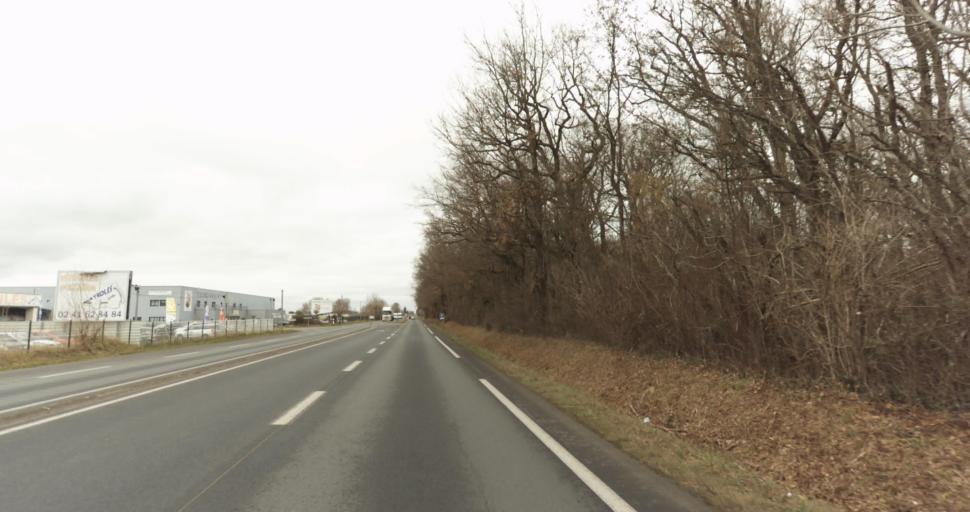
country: FR
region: Pays de la Loire
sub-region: Departement de Maine-et-Loire
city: Vivy
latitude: 47.3373
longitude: -0.0668
